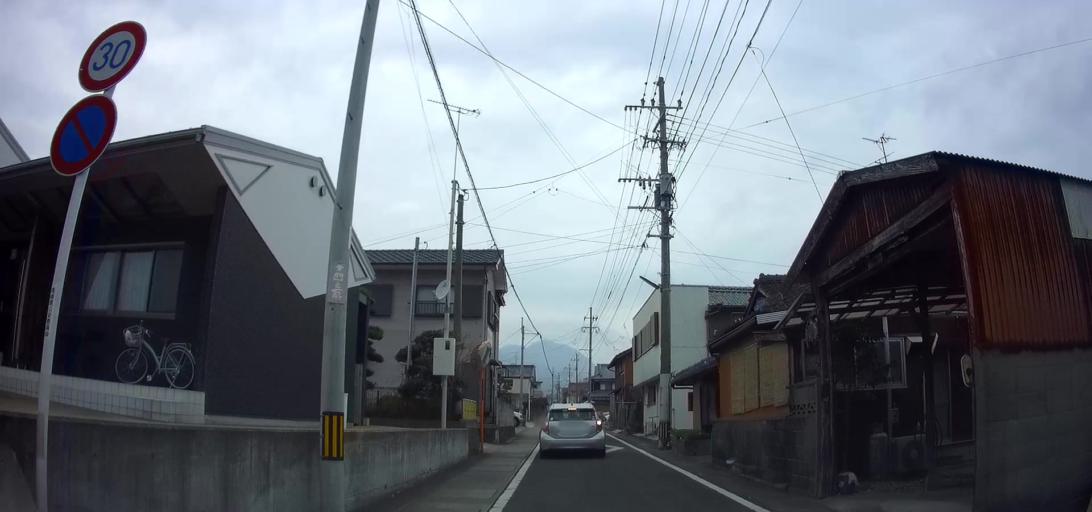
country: JP
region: Nagasaki
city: Shimabara
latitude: 32.6642
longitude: 130.3012
